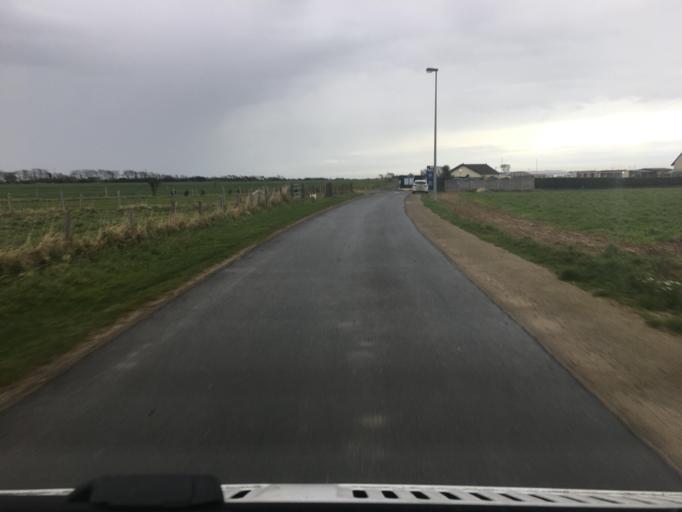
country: FR
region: Lower Normandy
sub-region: Departement du Calvados
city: Grandcamp-Maisy
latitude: 49.3782
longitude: -0.9100
